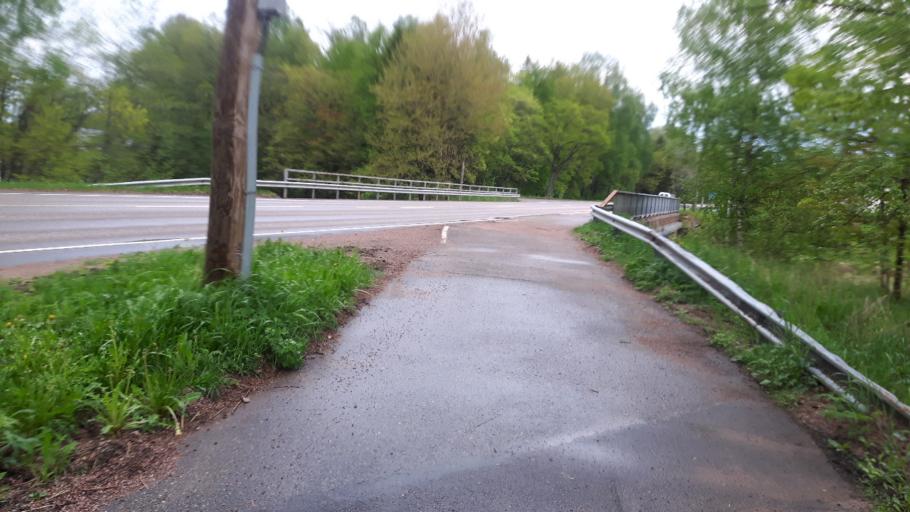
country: FI
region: Kymenlaakso
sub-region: Kotka-Hamina
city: Hamina
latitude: 60.5657
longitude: 27.0976
